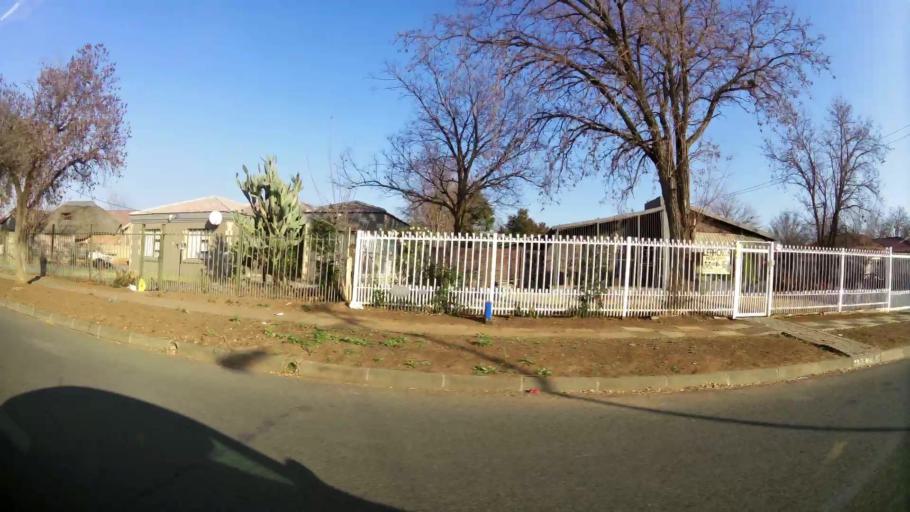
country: ZA
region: Orange Free State
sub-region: Mangaung Metropolitan Municipality
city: Bloemfontein
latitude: -29.1474
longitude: 26.2138
